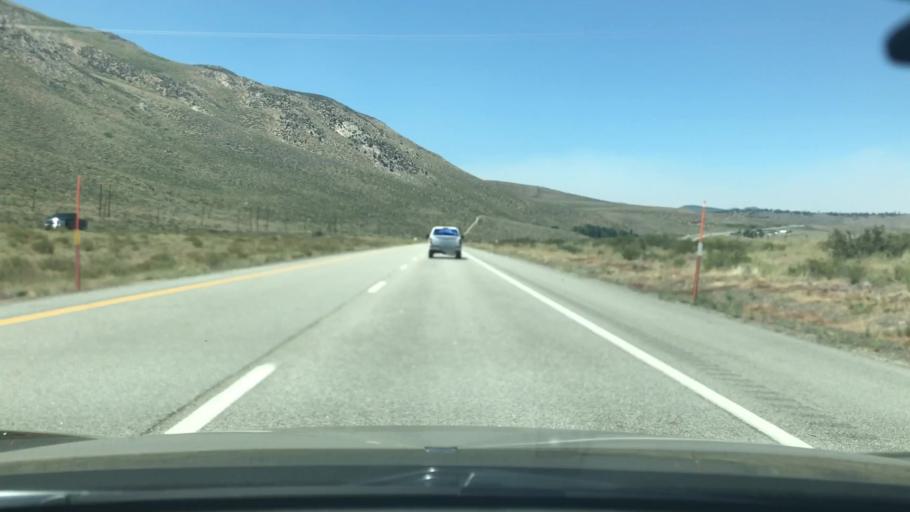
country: US
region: California
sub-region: Mono County
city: Mammoth Lakes
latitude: 37.5886
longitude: -118.7856
